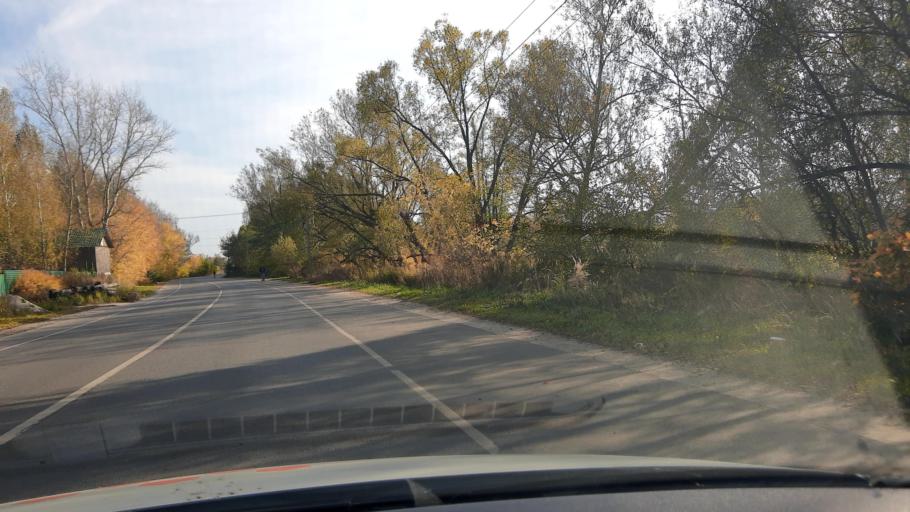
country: RU
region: Moskovskaya
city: Fryazevo
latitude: 55.7295
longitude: 38.4623
